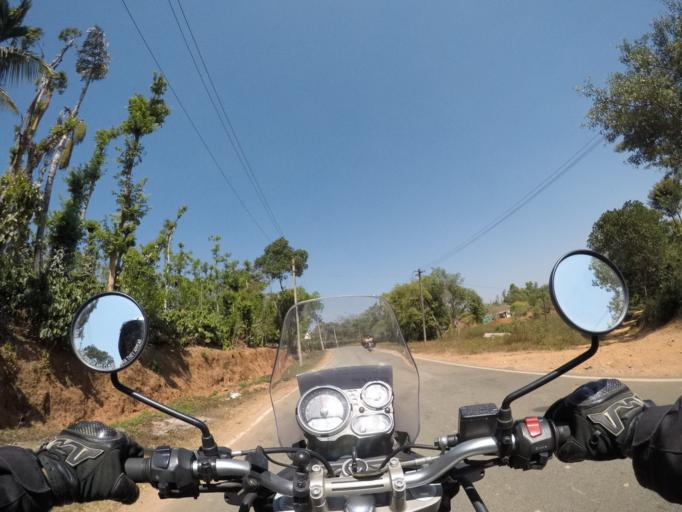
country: IN
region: Karnataka
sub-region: Hassan
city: Sakleshpur
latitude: 13.0213
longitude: 75.6980
